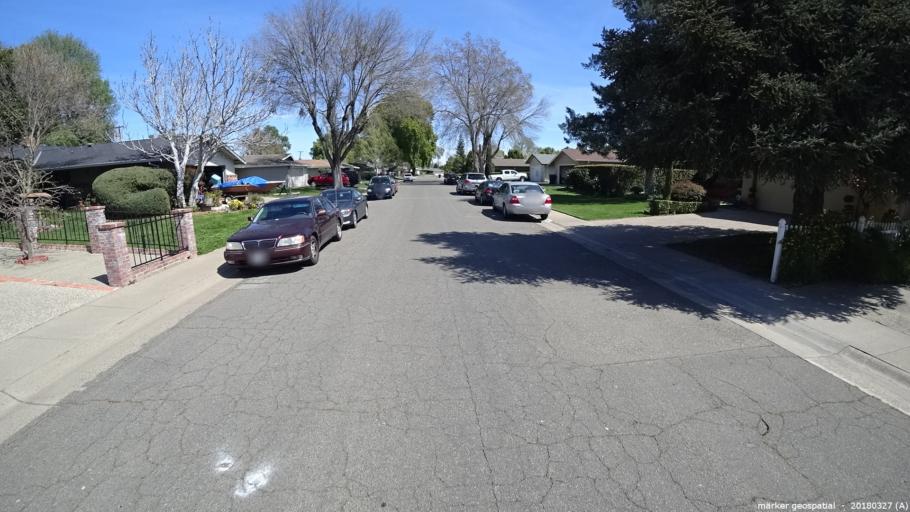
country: US
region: California
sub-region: Sacramento County
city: Rosemont
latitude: 38.5535
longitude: -121.3595
